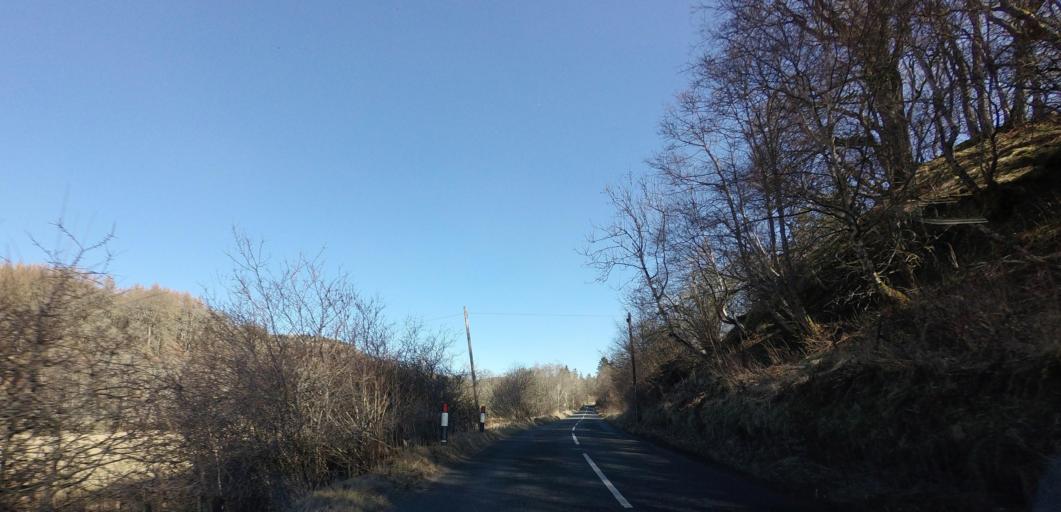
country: GB
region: Scotland
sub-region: Perth and Kinross
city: Methven
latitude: 56.5483
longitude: -3.6373
